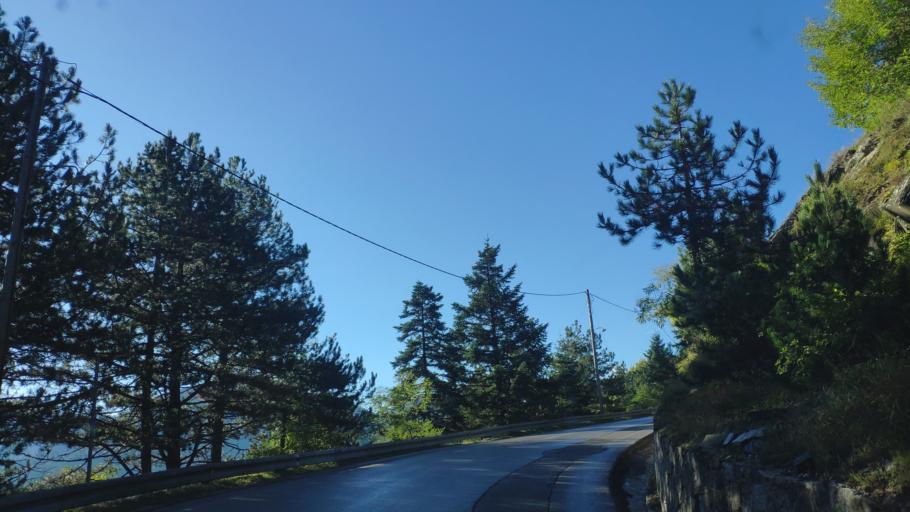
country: GR
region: Epirus
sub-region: Nomos Ioanninon
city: Metsovo
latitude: 39.7748
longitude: 21.1792
